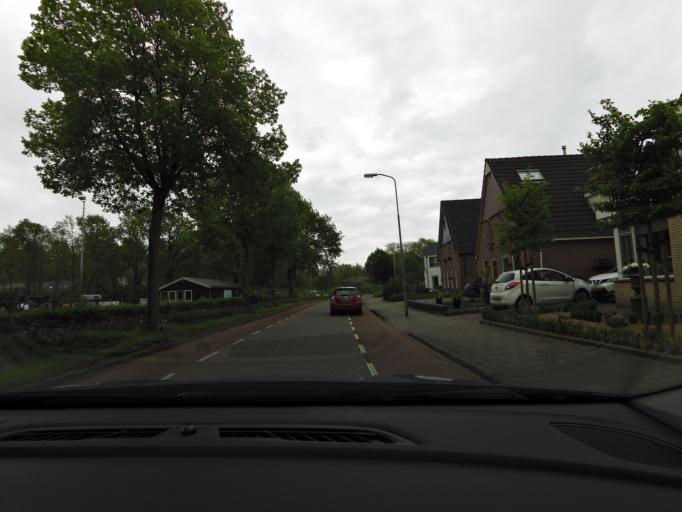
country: NL
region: South Holland
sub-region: Gemeente Leerdam
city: Leerdam
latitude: 51.8839
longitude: 5.1069
